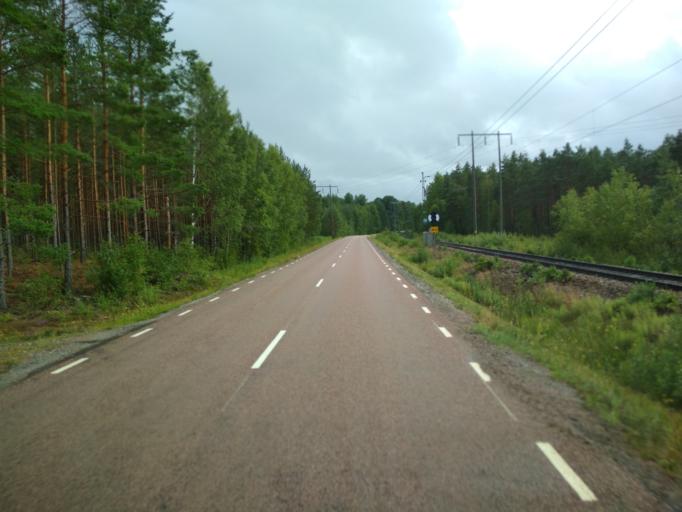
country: SE
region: Vaestmanland
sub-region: Surahammars Kommun
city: Ramnas
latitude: 59.8041
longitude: 16.1697
